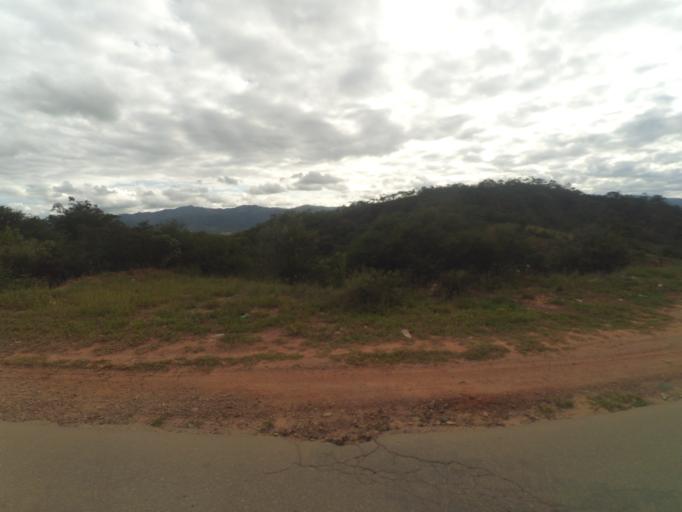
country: BO
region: Santa Cruz
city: Samaipata
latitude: -18.1651
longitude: -63.9064
